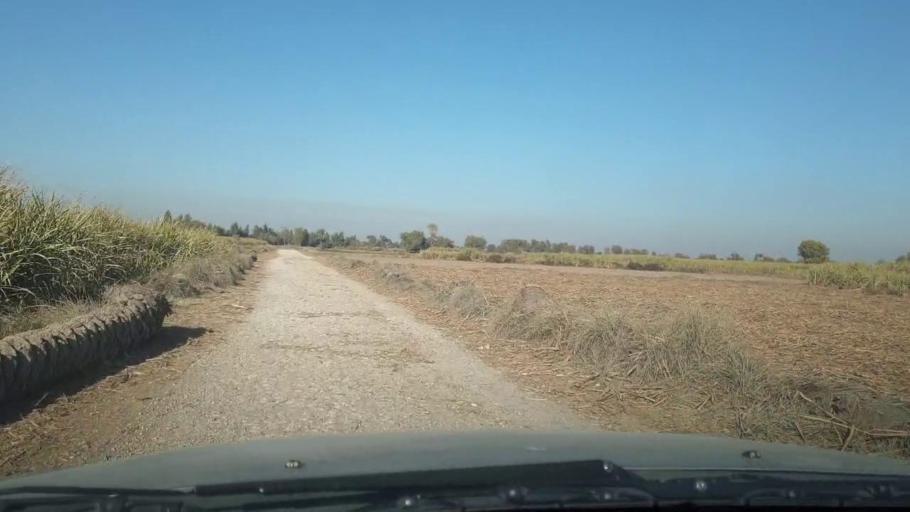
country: PK
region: Sindh
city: Adilpur
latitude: 27.9528
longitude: 69.1982
